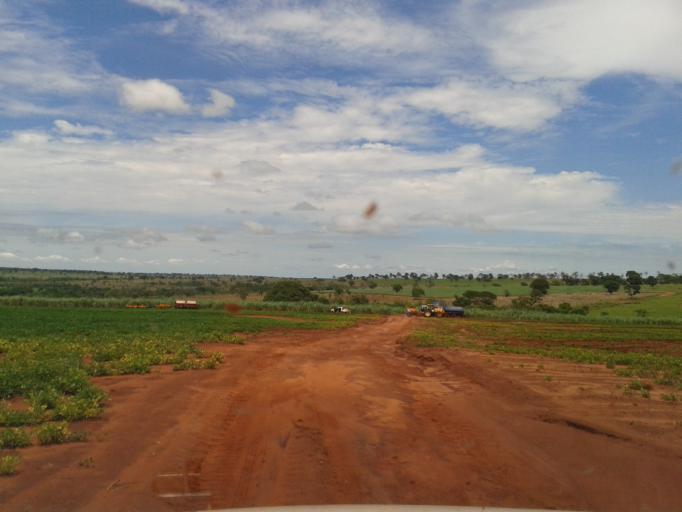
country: BR
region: Minas Gerais
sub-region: Santa Vitoria
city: Santa Vitoria
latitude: -19.2092
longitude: -50.6330
